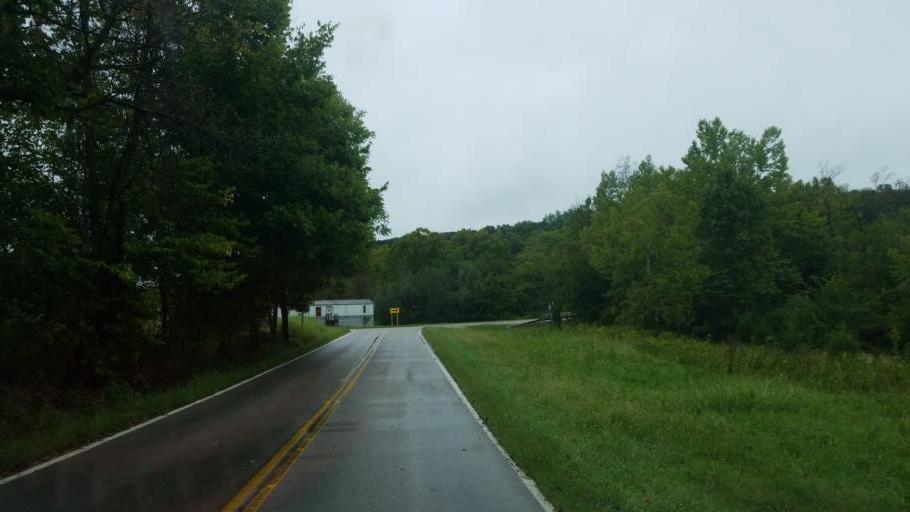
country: US
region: Ohio
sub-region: Adams County
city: West Union
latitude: 38.7504
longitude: -83.5163
